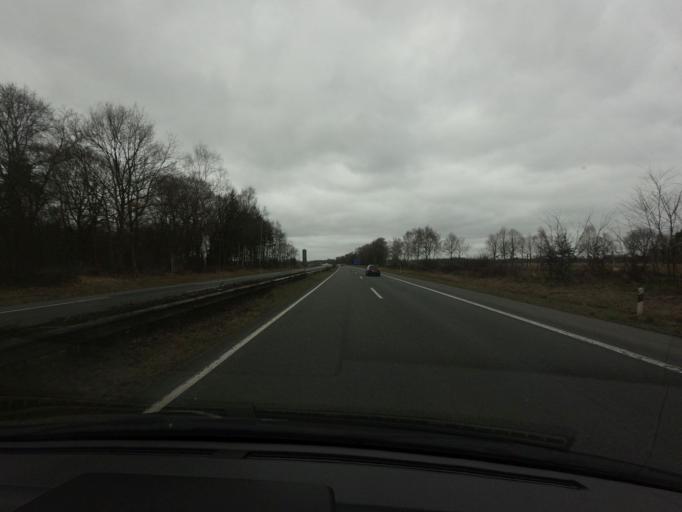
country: DE
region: Lower Saxony
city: Wiefelstede
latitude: 53.1951
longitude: 8.0973
